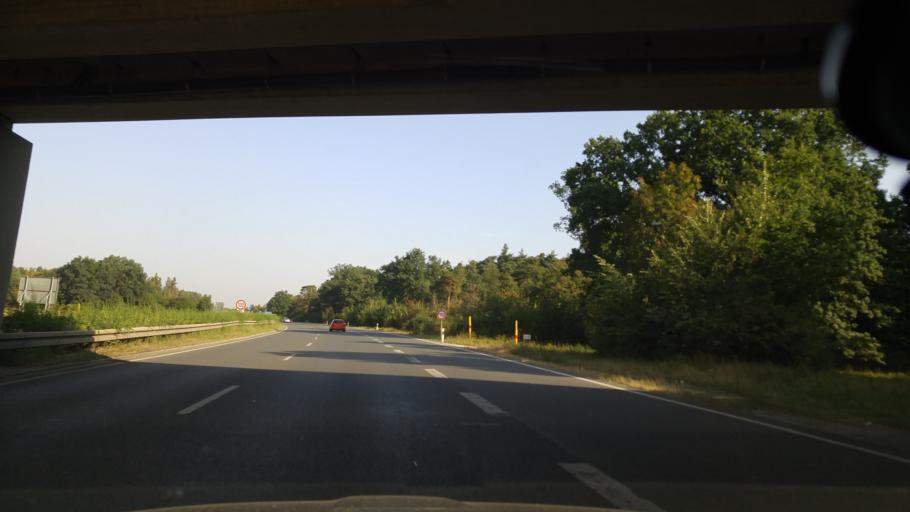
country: DE
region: Bavaria
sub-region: Regierungsbezirk Mittelfranken
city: Wetzendorf
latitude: 49.5317
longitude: 11.0333
